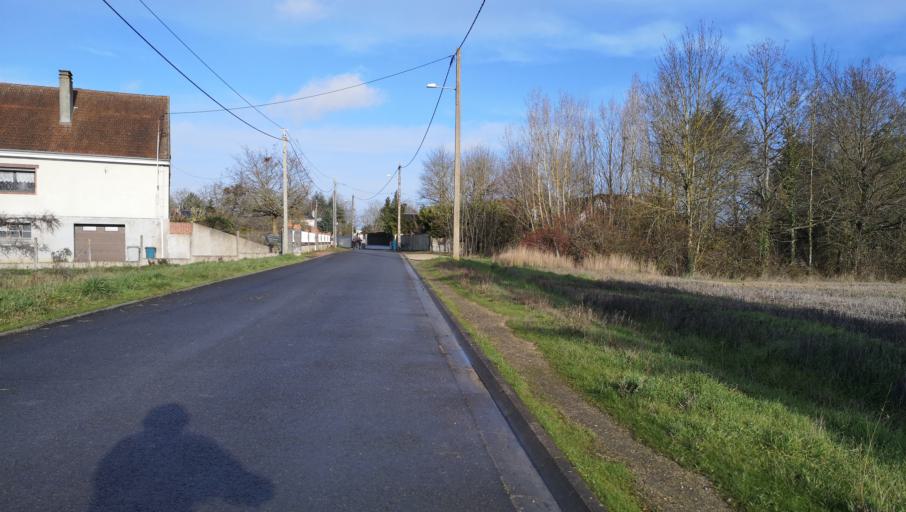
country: FR
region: Centre
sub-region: Departement du Loiret
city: Saint-Pryve-Saint-Mesmin
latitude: 47.8745
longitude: 1.8543
